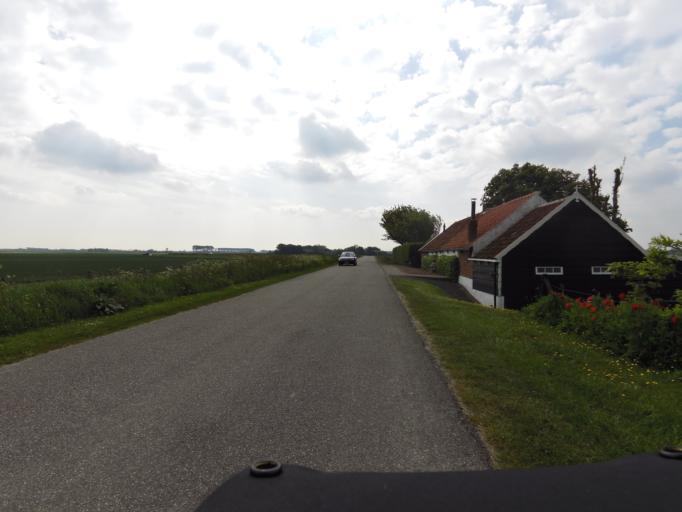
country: NL
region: Zeeland
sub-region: Gemeente Noord-Beveland
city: Kamperland
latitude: 51.5838
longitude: 3.7010
